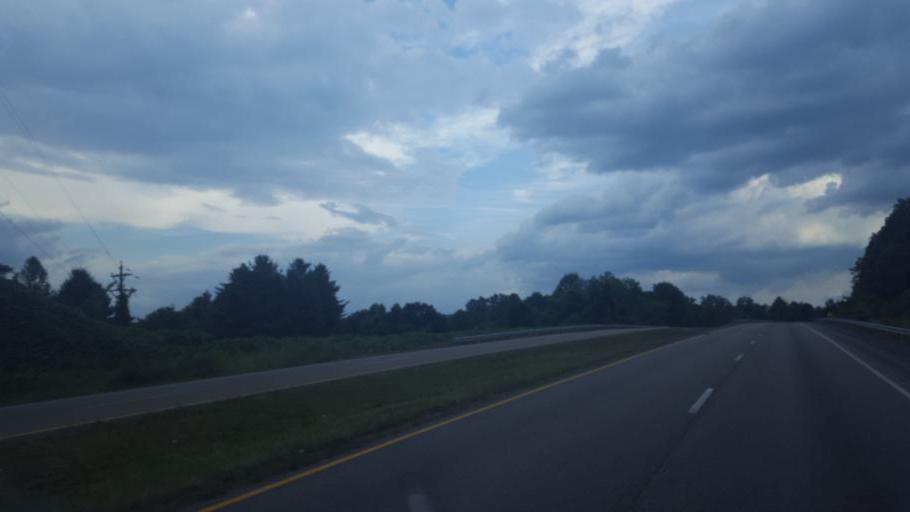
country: US
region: Virginia
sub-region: Wise County
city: Pound
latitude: 37.1130
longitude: -82.6074
